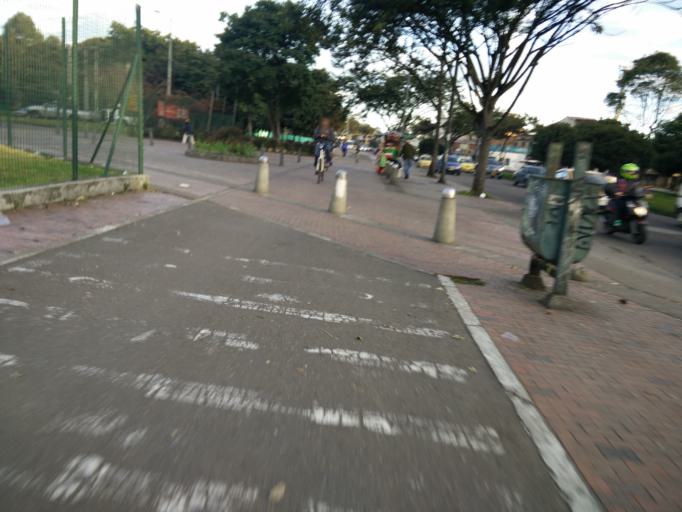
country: CO
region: Bogota D.C.
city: Bogota
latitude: 4.6670
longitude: -74.0955
